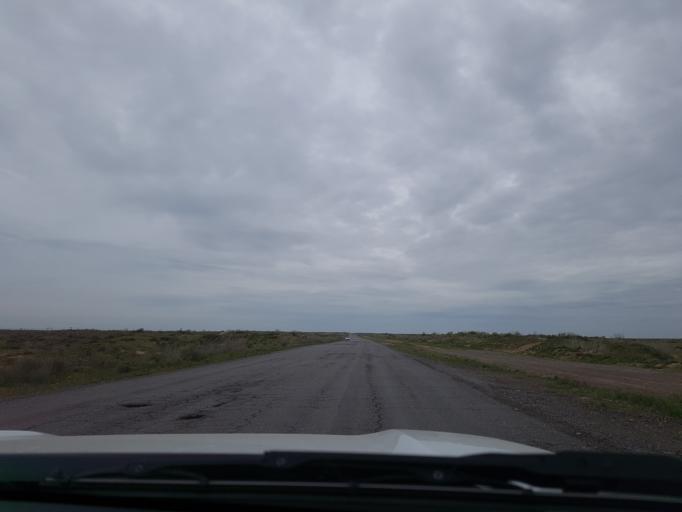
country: TM
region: Mary
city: Bayramaly
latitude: 38.0667
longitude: 62.7735
